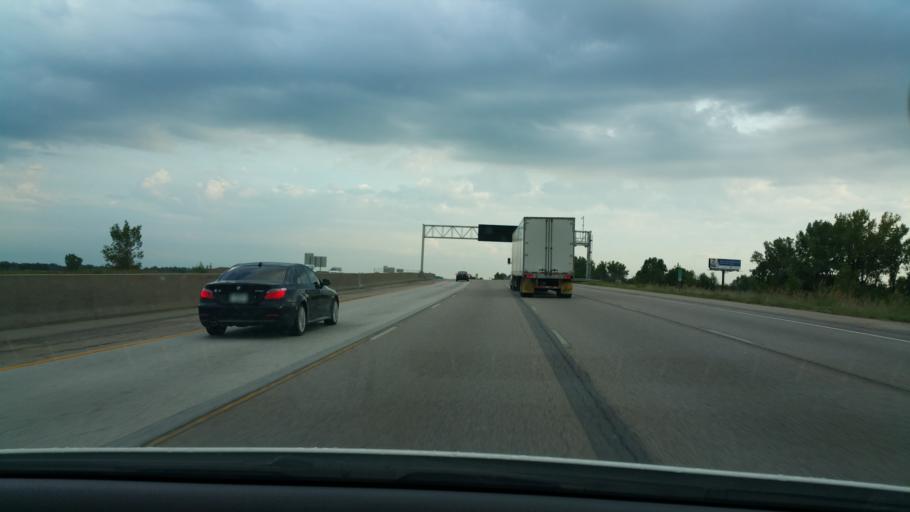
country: US
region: Iowa
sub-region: Polk County
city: Saylorville
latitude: 41.6713
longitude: -93.5778
